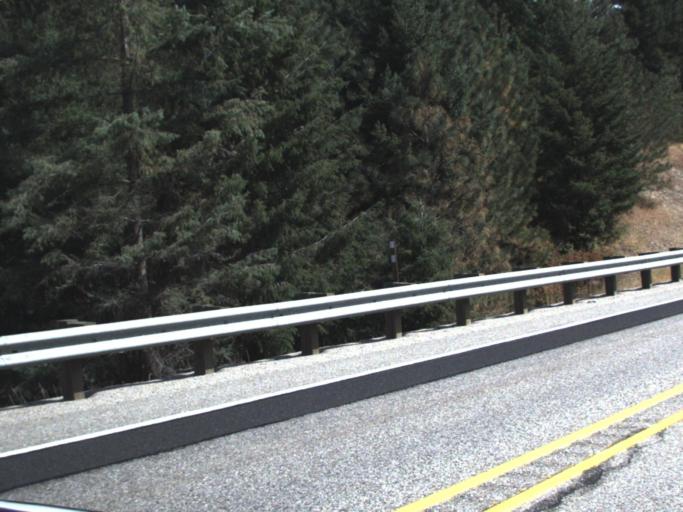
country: US
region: Washington
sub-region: Stevens County
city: Chewelah
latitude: 48.1426
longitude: -117.6621
